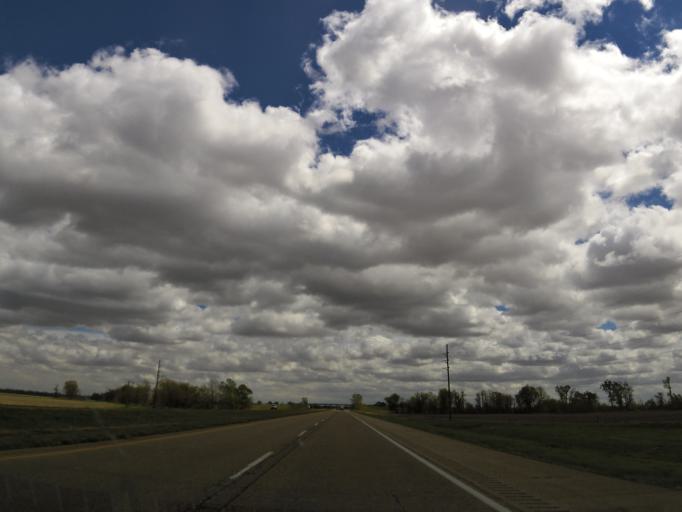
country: US
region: Arkansas
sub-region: Poinsett County
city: Trumann
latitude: 35.6500
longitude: -90.5256
